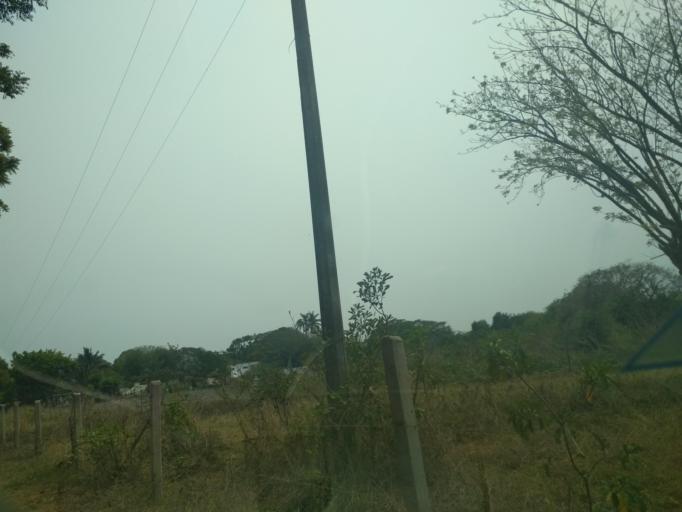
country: MX
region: Veracruz
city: El Tejar
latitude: 19.0654
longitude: -96.1538
